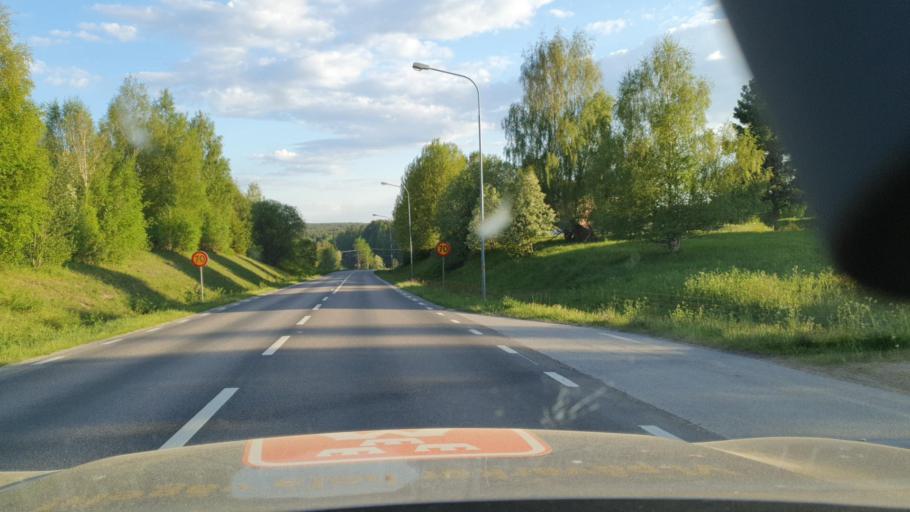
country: SE
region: Vaesternorrland
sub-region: Solleftea Kommun
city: As
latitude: 63.6939
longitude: 16.8772
